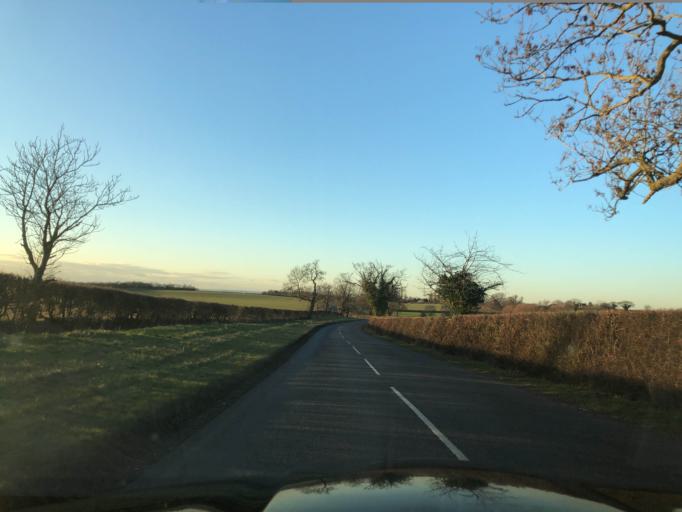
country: GB
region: England
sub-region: Warwickshire
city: Harbury
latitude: 52.2282
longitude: -1.4680
